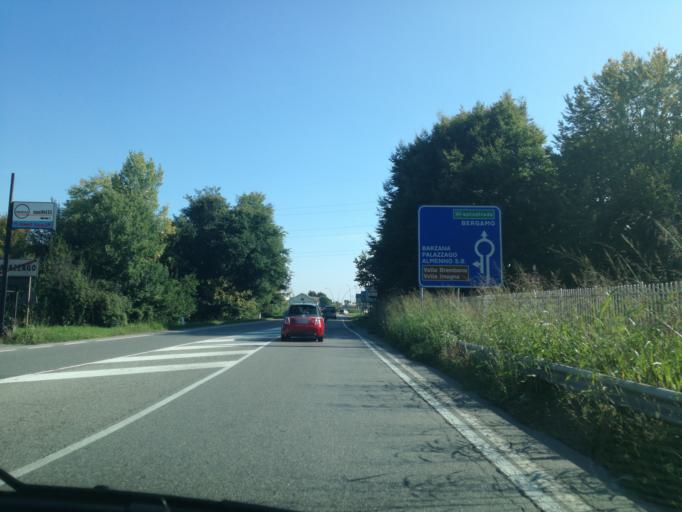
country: IT
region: Lombardy
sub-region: Provincia di Bergamo
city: Ambivere
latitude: 45.7260
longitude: 9.5500
